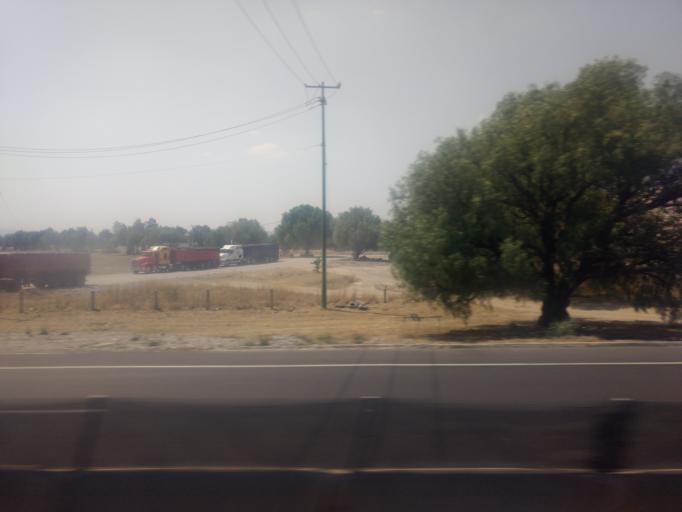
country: MX
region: Morelos
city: San Martin de las Piramides
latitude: 19.6749
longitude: -98.8235
